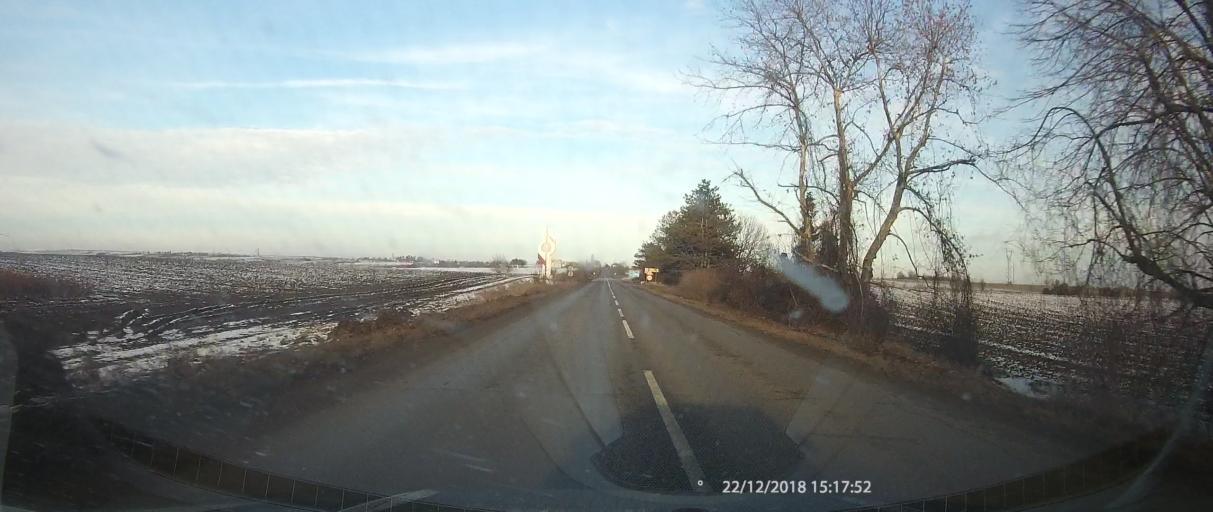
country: BG
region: Ruse
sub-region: Obshtina Dve Mogili
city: Dve Mogili
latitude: 43.6314
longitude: 25.8654
